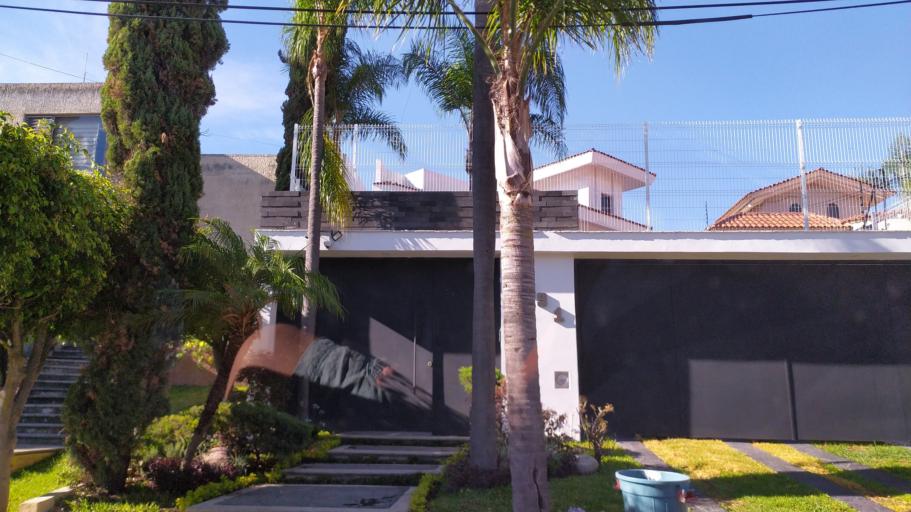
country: MX
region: Jalisco
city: Guadalajara
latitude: 20.6610
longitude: -103.4253
